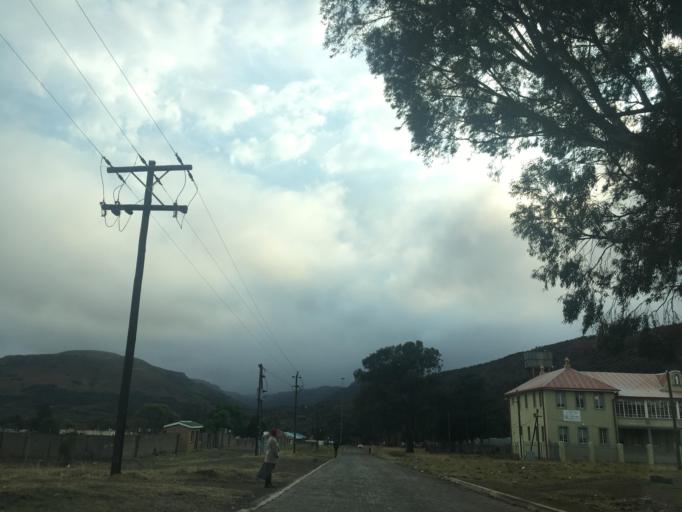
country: ZA
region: Eastern Cape
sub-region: Chris Hani District Municipality
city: Cala
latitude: -31.5248
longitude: 27.6981
